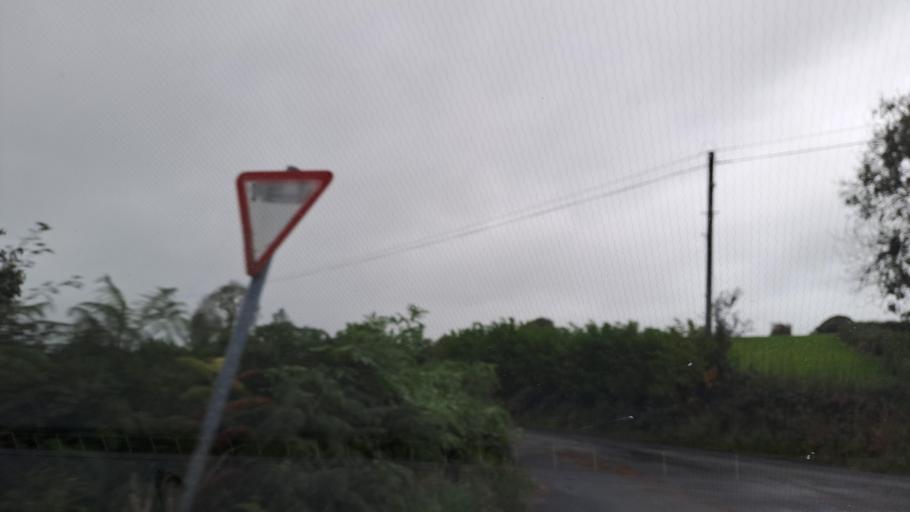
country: IE
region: Ulster
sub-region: An Cabhan
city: Kingscourt
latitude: 54.0026
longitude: -6.8551
